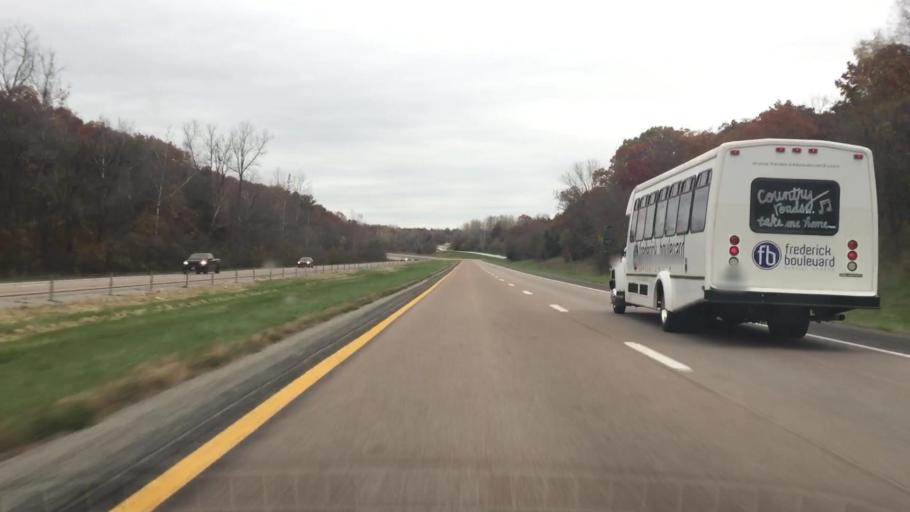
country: US
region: Missouri
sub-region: Cole County
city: Jefferson City
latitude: 38.6634
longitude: -92.2259
